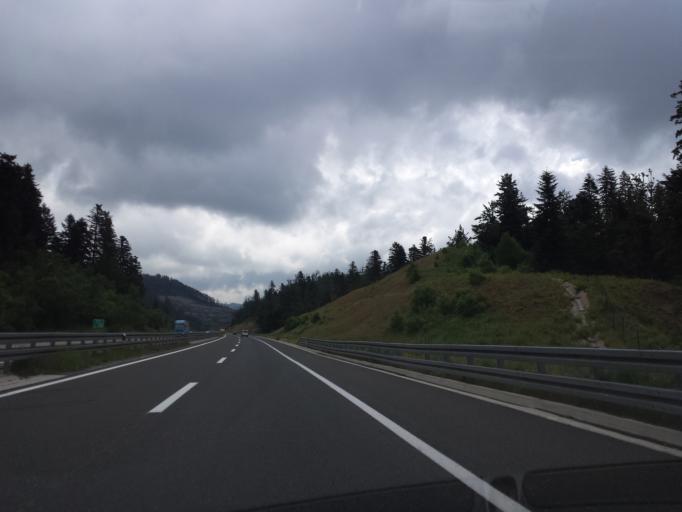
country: HR
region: Primorsko-Goranska
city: Hreljin
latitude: 45.3157
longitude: 14.6981
